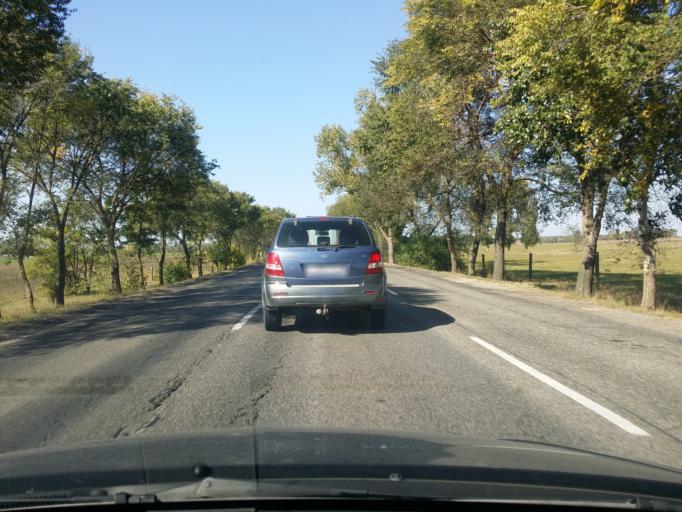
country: HU
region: Bacs-Kiskun
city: Nyarlorinc
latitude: 46.9093
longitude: 19.8077
